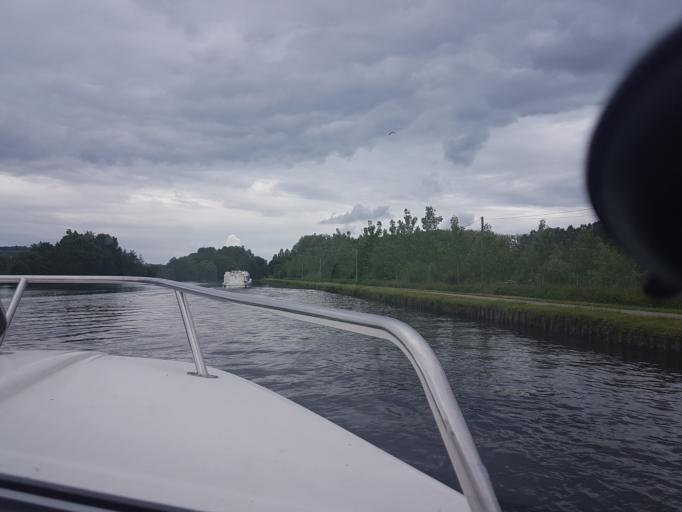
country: FR
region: Bourgogne
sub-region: Departement de l'Yonne
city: Champs-sur-Yonne
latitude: 47.7302
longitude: 3.6035
